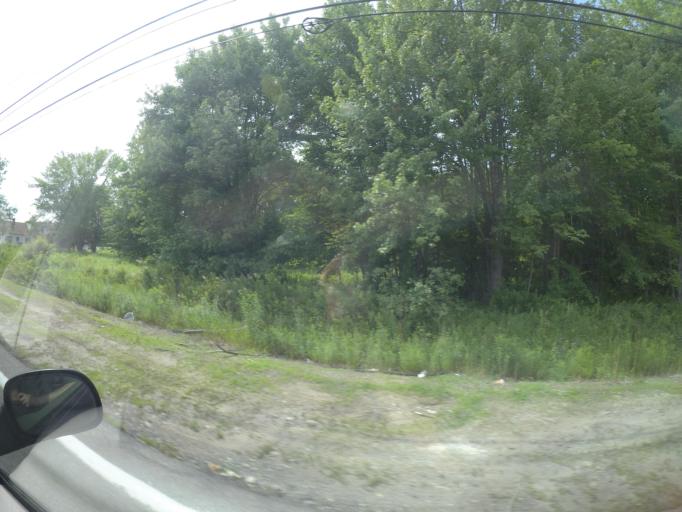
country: US
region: Maine
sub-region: Cumberland County
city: West Scarborough
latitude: 43.5429
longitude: -70.4160
